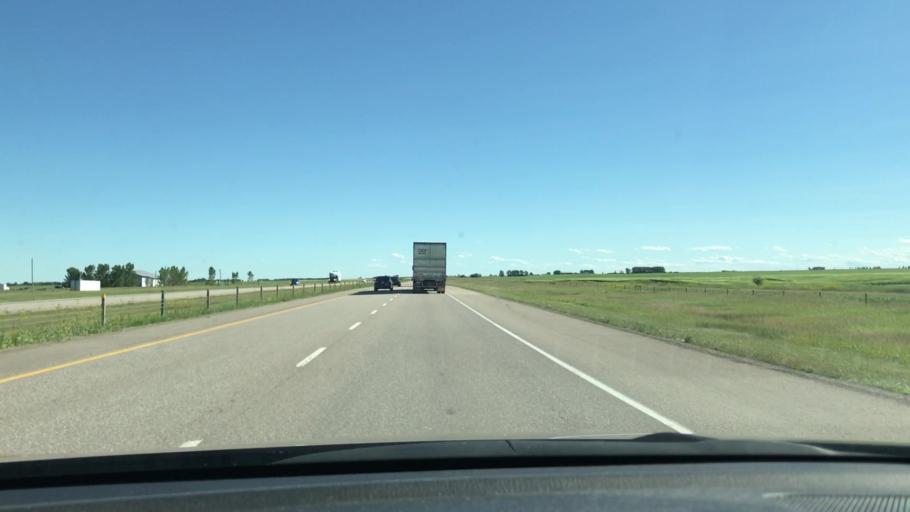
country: CA
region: Alberta
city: Olds
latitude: 51.7050
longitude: -114.0256
